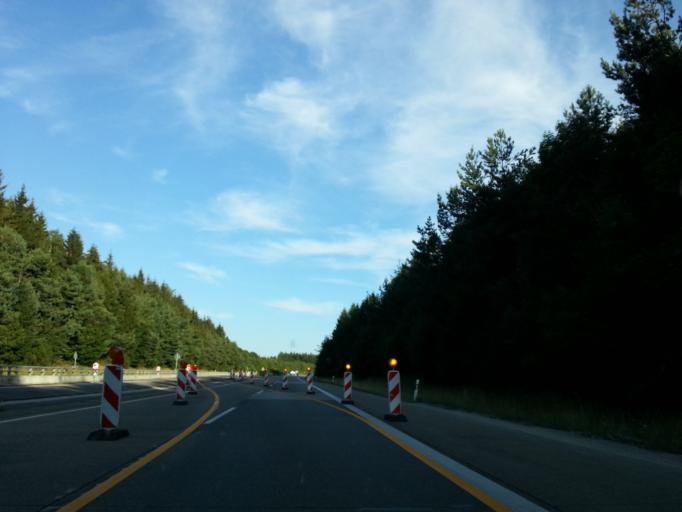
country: DE
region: Rheinland-Pfalz
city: Bescheid
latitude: 49.7405
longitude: 6.8804
